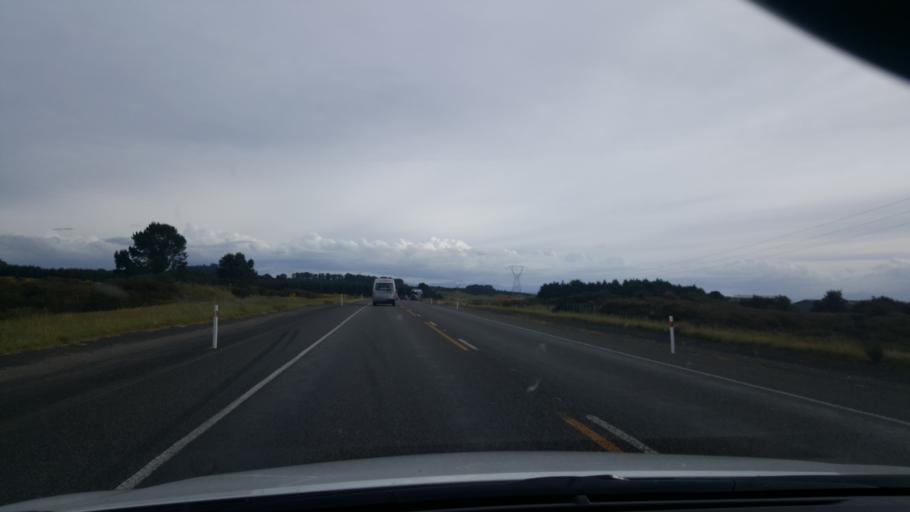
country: NZ
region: Waikato
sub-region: Taupo District
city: Taupo
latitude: -38.6923
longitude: 176.1138
